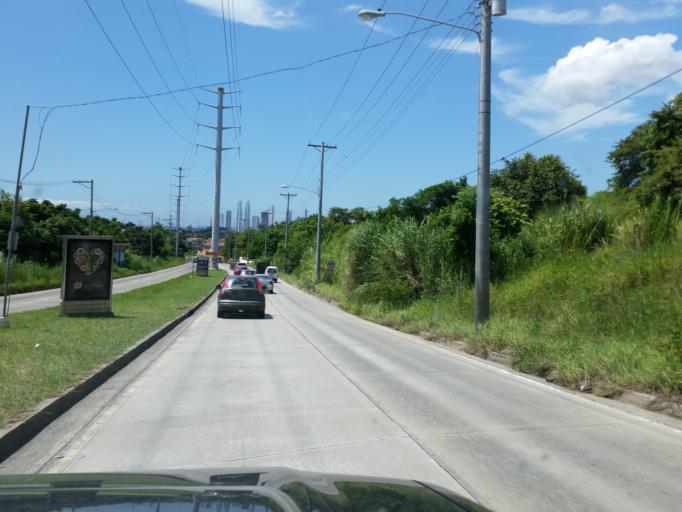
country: PA
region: Panama
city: San Miguelito
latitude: 9.0630
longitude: -79.4621
